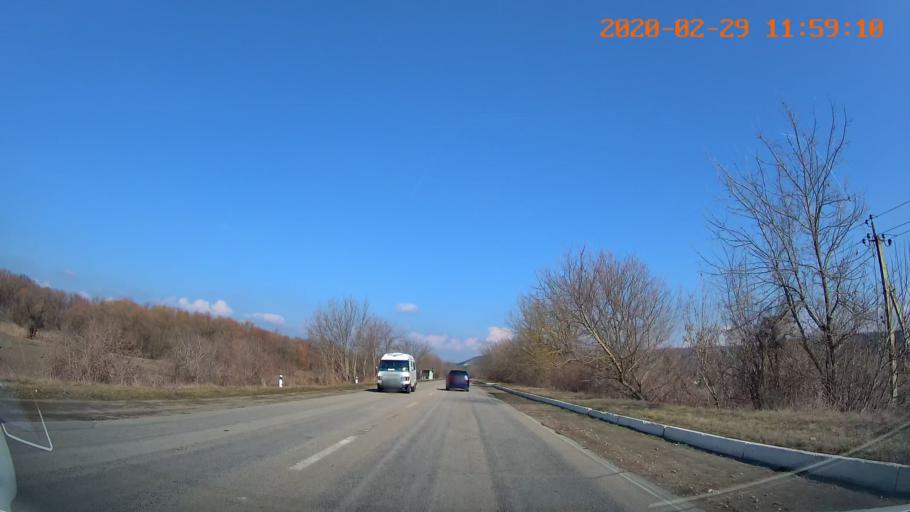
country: MD
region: Telenesti
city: Ribnita
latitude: 47.8219
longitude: 29.0154
